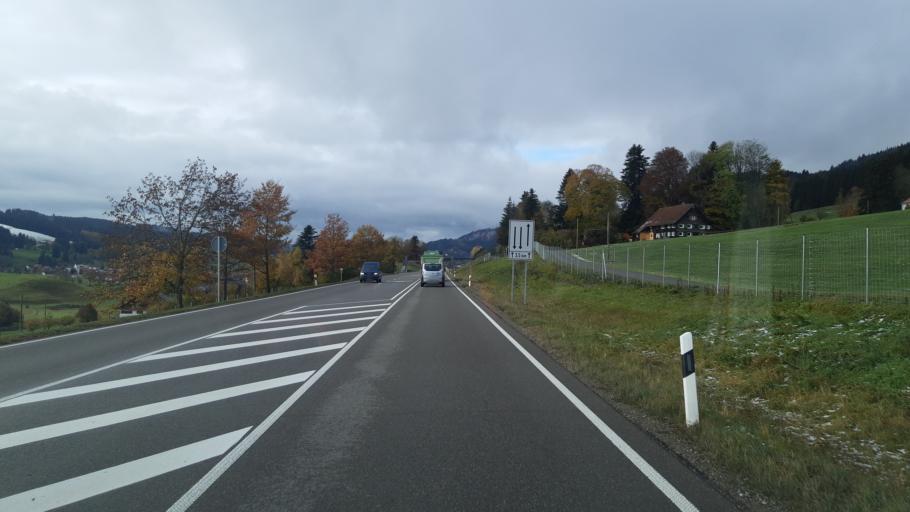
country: DE
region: Bavaria
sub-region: Swabia
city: Weitnau
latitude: 47.6496
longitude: 10.1433
